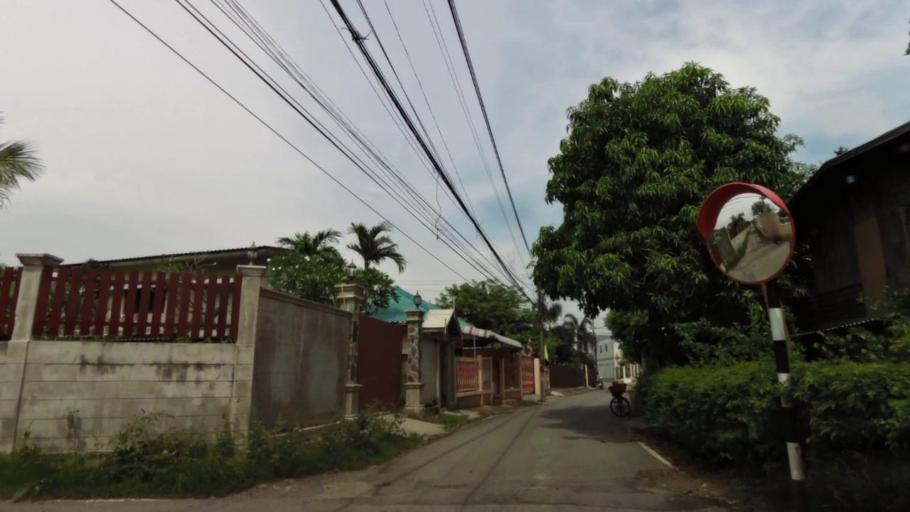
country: TH
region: Lop Buri
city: Ban Mi
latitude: 15.0472
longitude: 100.5666
